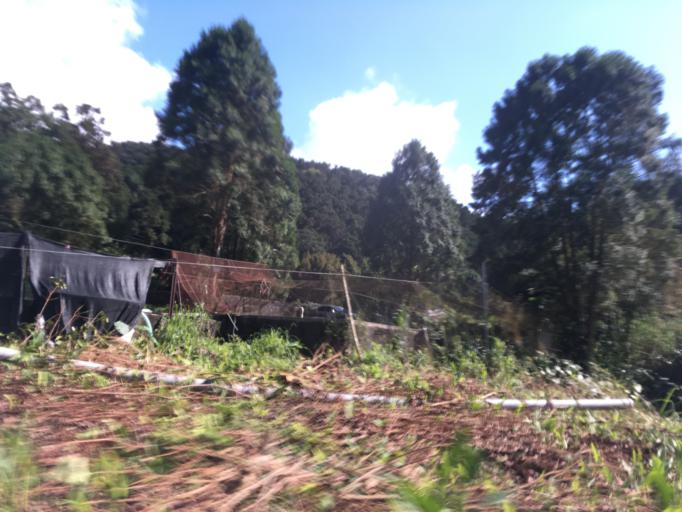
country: TW
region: Taiwan
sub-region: Yilan
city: Yilan
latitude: 24.7544
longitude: 121.6233
